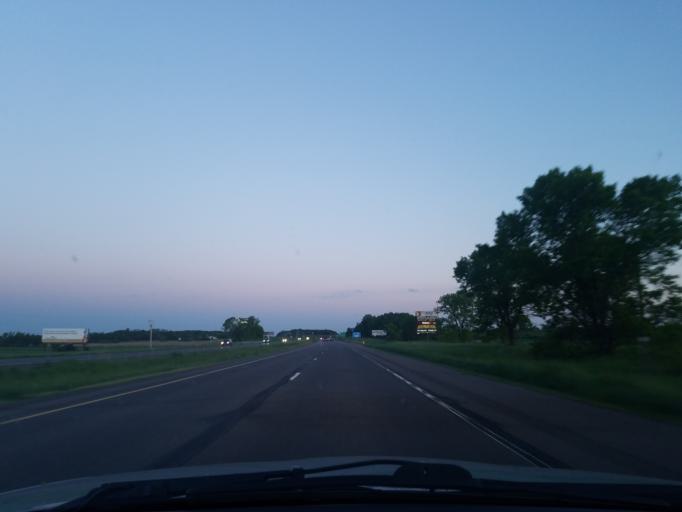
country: US
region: Minnesota
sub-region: Pine County
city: Rock Creek
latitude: 45.7760
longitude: -92.9905
